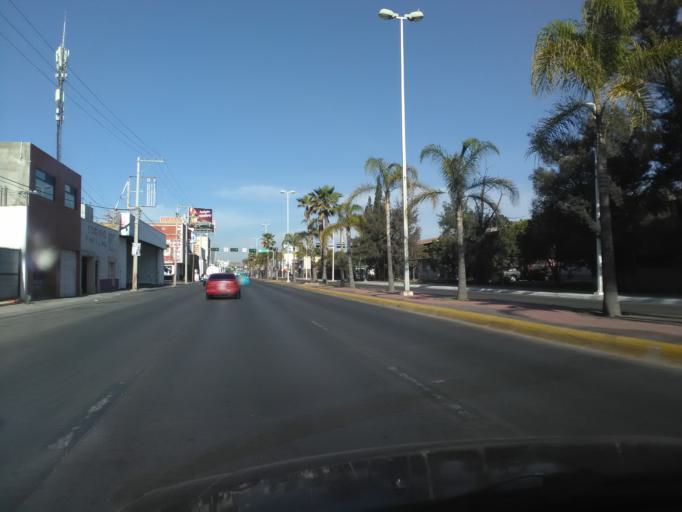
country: MX
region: Durango
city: Victoria de Durango
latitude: 24.0353
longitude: -104.6637
